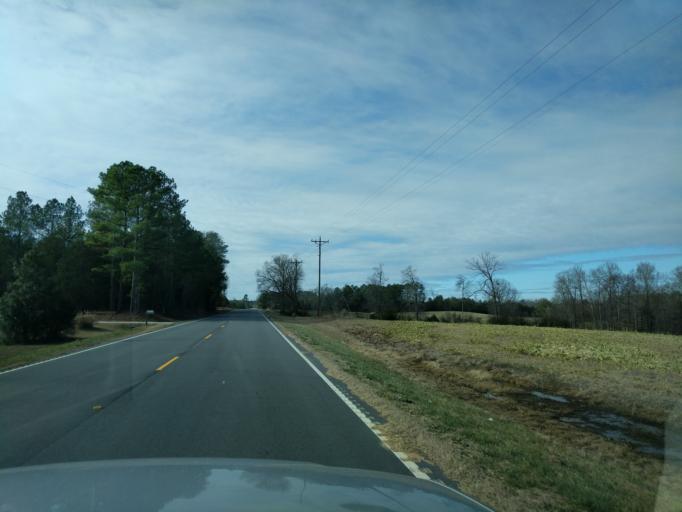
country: US
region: South Carolina
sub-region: Edgefield County
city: Edgefield
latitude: 33.9363
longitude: -81.9558
